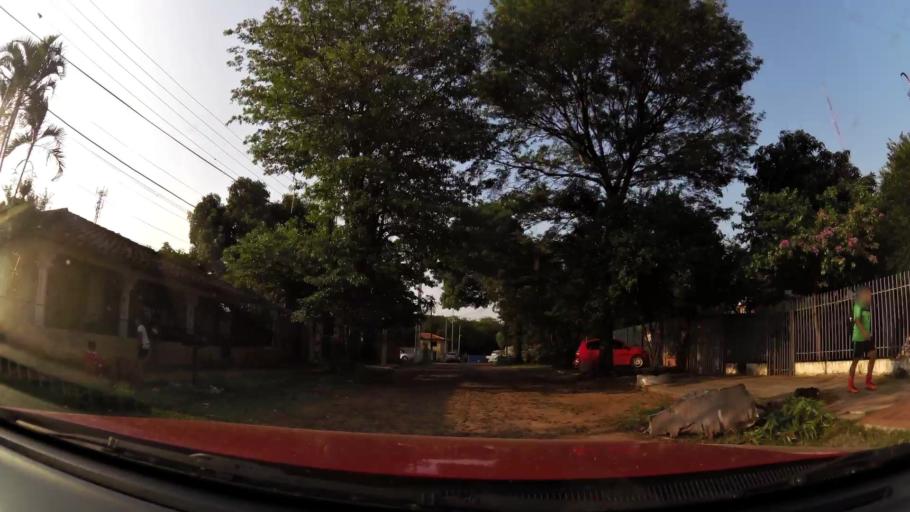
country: PY
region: Central
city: Lambare
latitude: -25.3576
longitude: -57.6014
